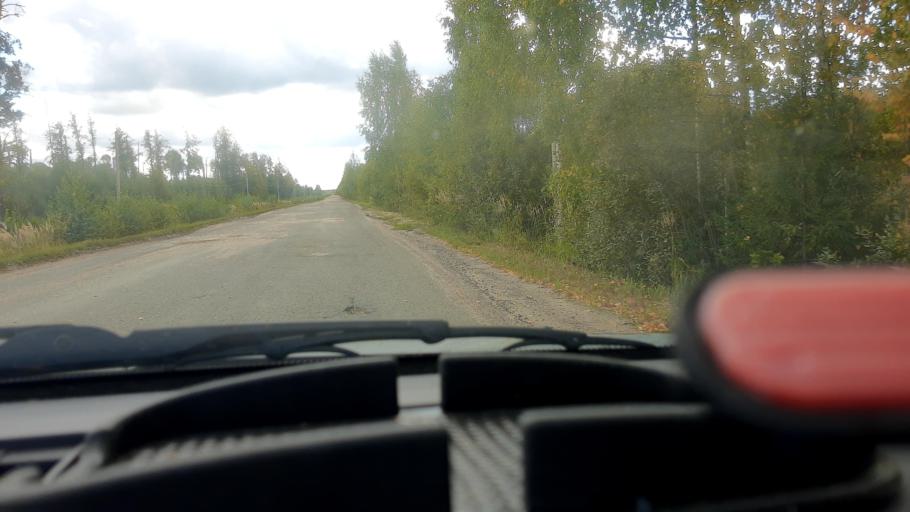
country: RU
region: Mariy-El
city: Kilemary
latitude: 56.8978
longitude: 46.7466
